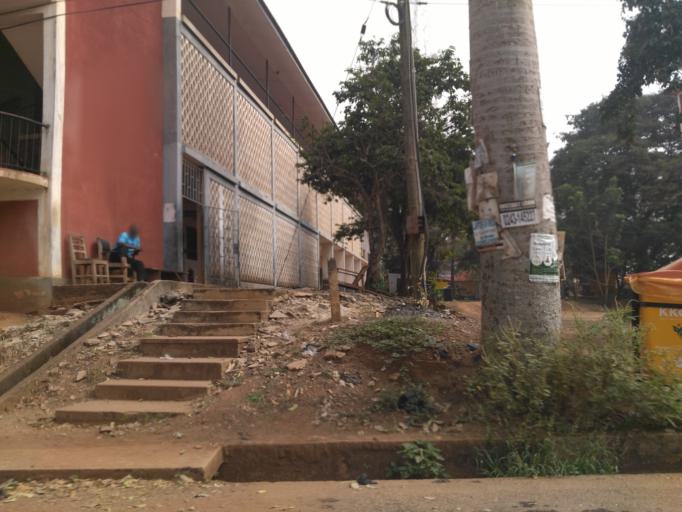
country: GH
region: Ashanti
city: Kumasi
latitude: 6.6905
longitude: -1.6250
